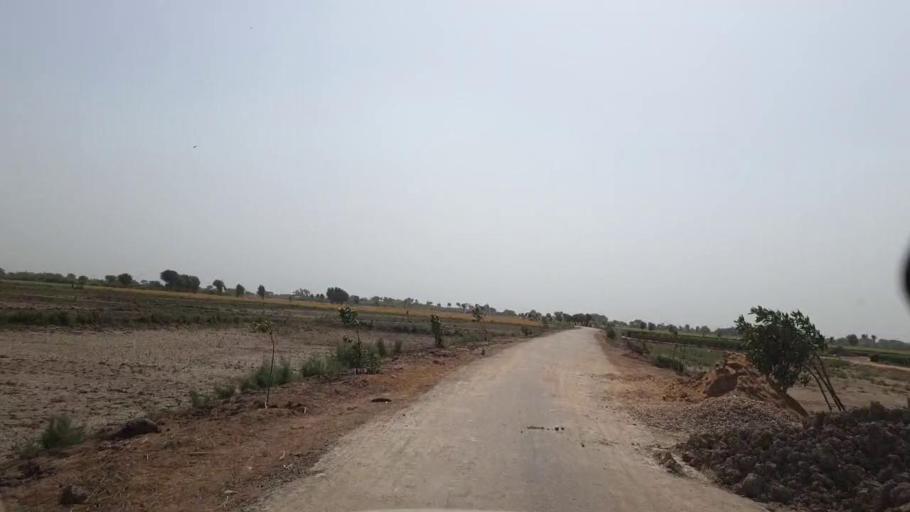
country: PK
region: Sindh
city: Matli
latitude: 25.0473
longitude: 68.6840
